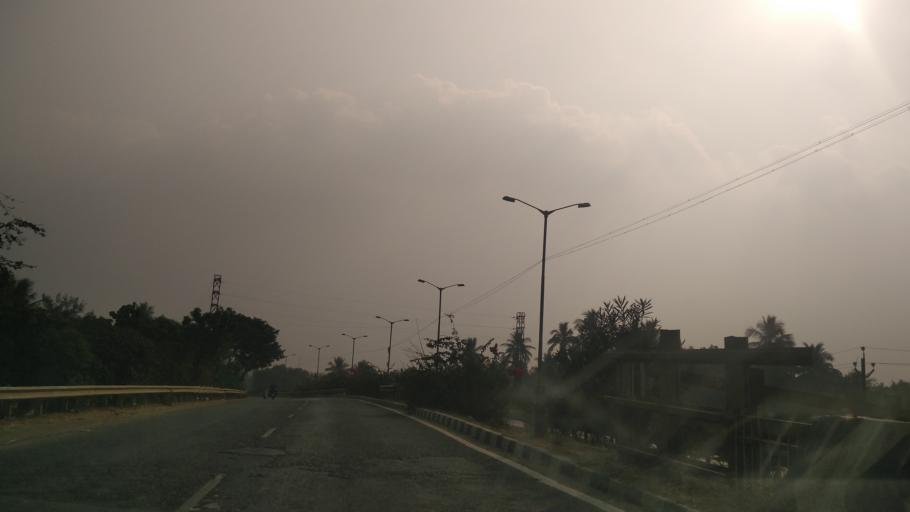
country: IN
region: Andhra Pradesh
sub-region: East Godavari
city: Rajahmundry
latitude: 16.9572
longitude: 81.7933
